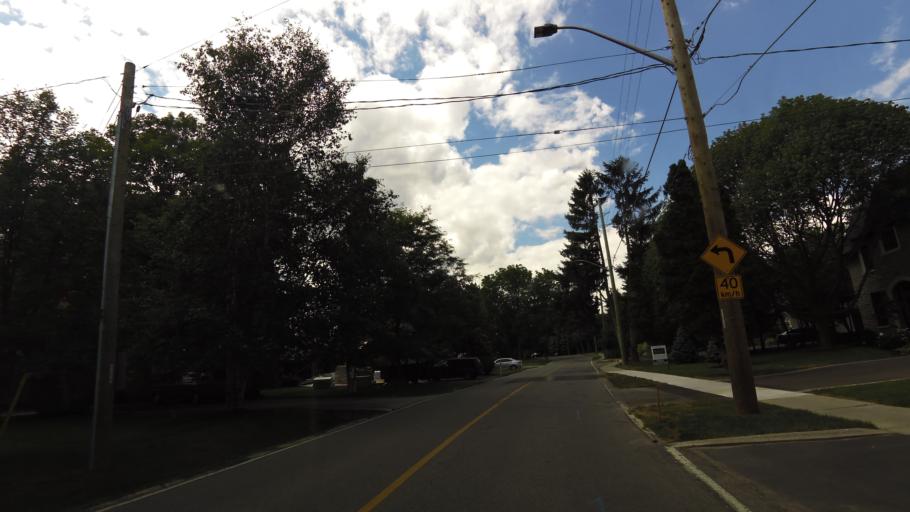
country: CA
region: Ontario
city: Mississauga
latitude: 43.5122
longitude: -79.6077
